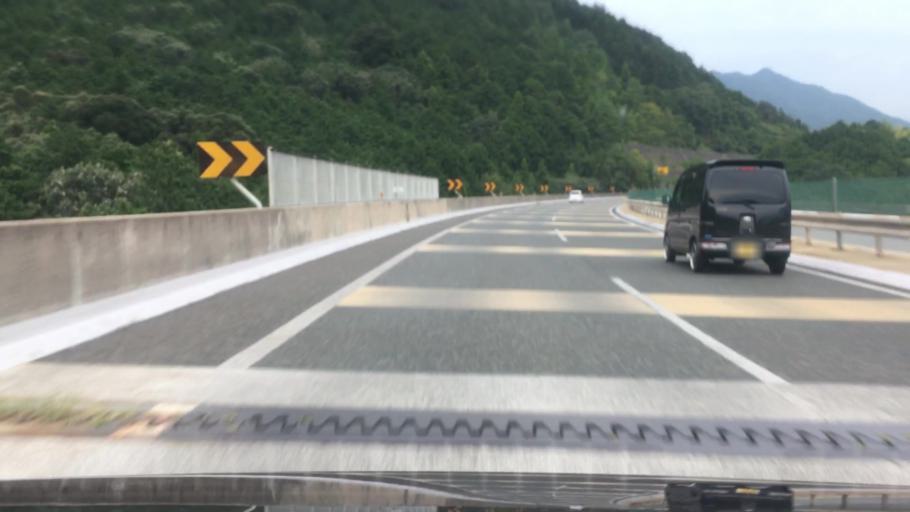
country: JP
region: Hyogo
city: Sasayama
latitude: 35.1380
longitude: 135.1408
